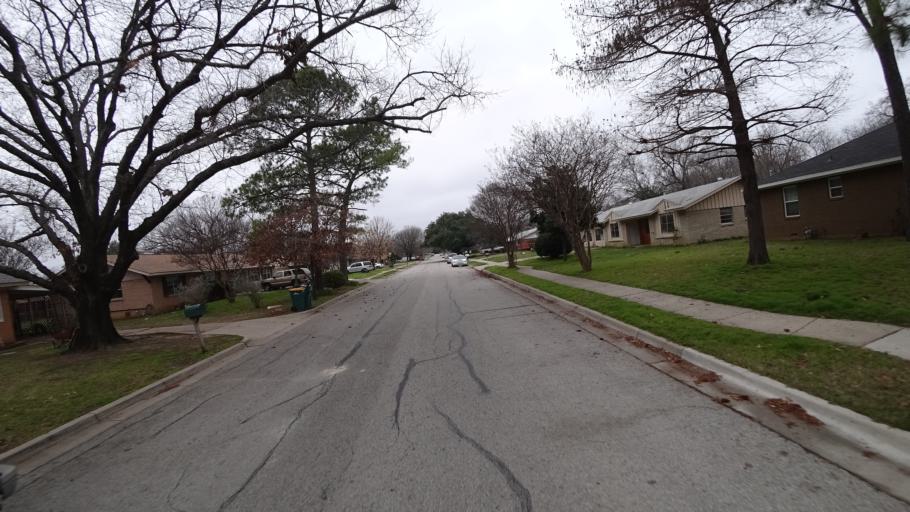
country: US
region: Texas
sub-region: Denton County
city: Lewisville
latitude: 33.0621
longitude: -97.0051
